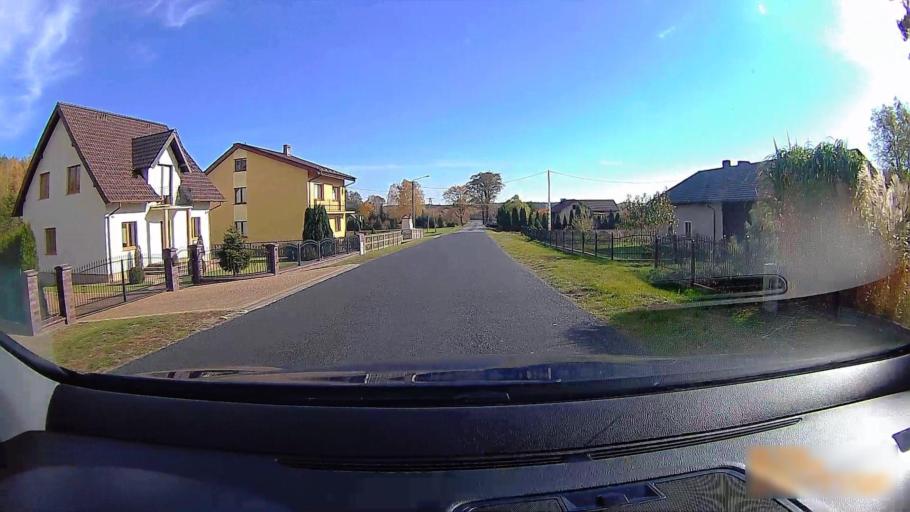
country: PL
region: Greater Poland Voivodeship
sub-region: Powiat ostrzeszowski
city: Ostrzeszow
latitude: 51.4130
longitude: 17.9797
